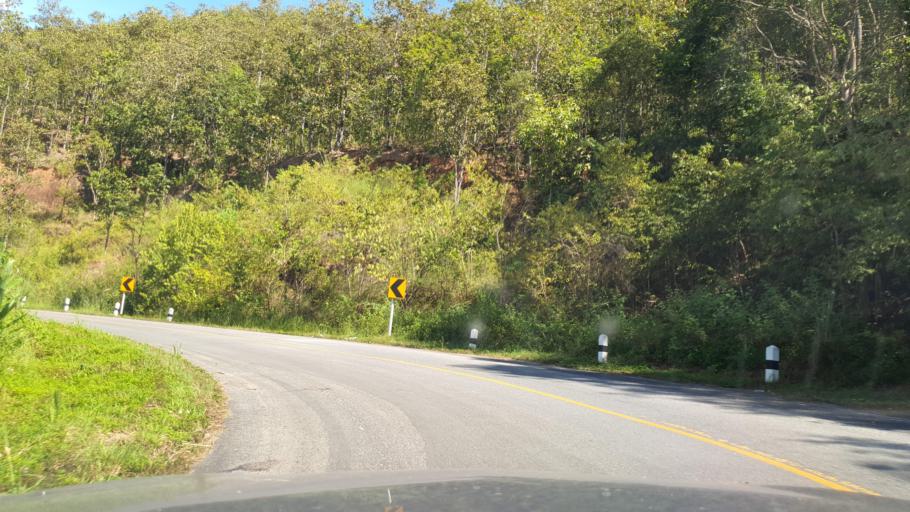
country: TH
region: Chiang Mai
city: Phrao
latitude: 19.3689
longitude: 99.2464
